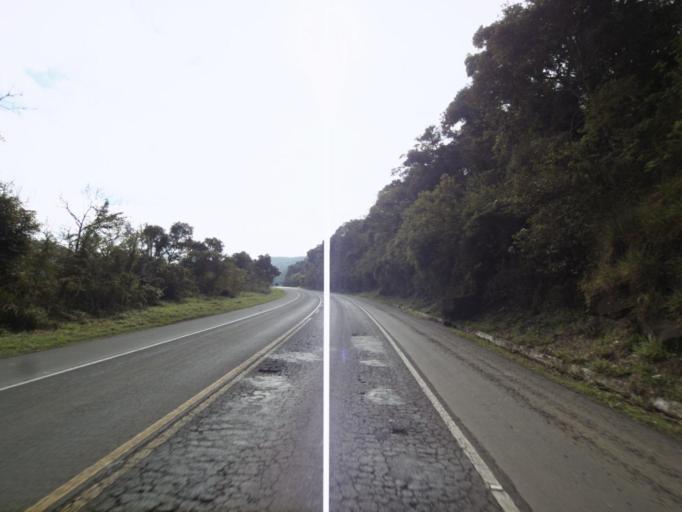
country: BR
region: Rio Grande do Sul
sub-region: Frederico Westphalen
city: Frederico Westphalen
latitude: -27.1522
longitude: -53.2156
